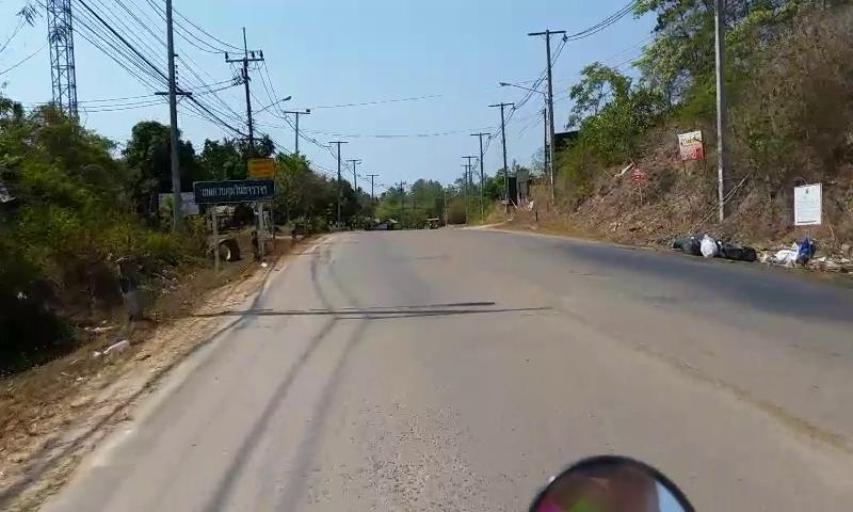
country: TH
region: Krabi
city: Saladan
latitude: 7.6202
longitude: 99.0321
